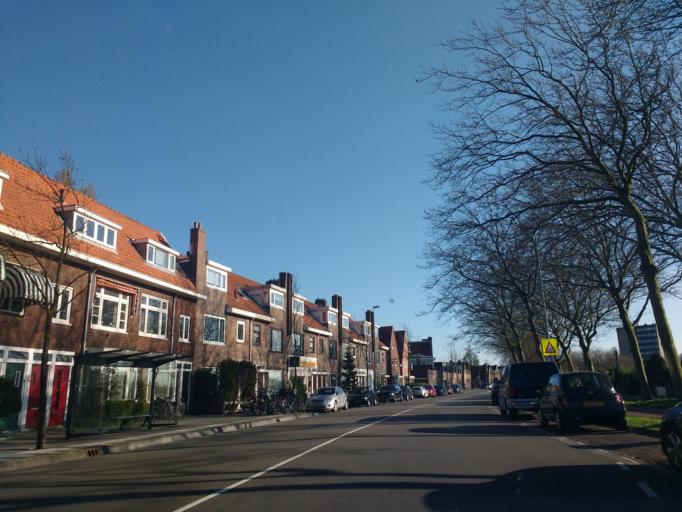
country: NL
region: North Holland
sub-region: Gemeente Haarlem
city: Haarlem
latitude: 52.3745
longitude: 4.6436
